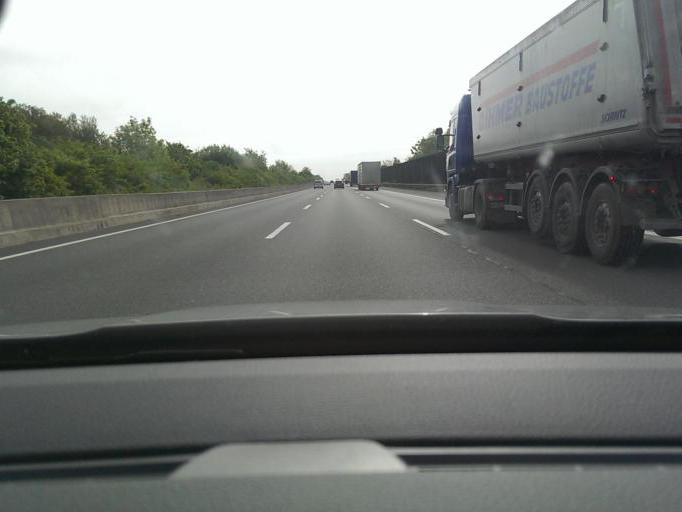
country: DE
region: Lower Saxony
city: Wendeburg
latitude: 52.3379
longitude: 10.3903
